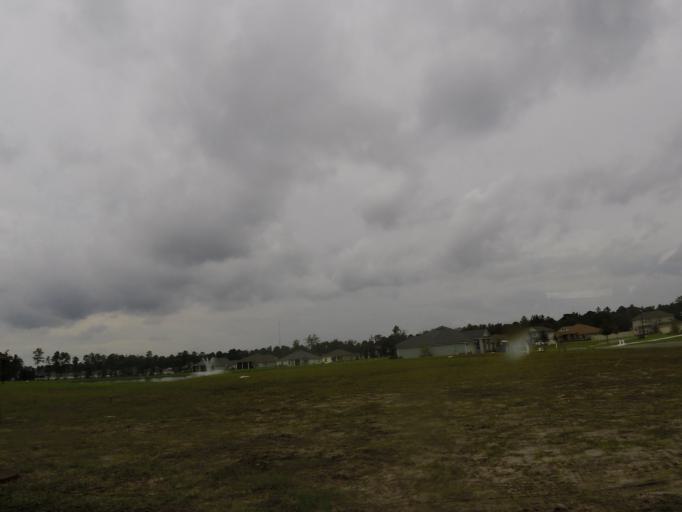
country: US
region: Florida
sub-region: Clay County
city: Middleburg
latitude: 30.1095
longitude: -81.8580
